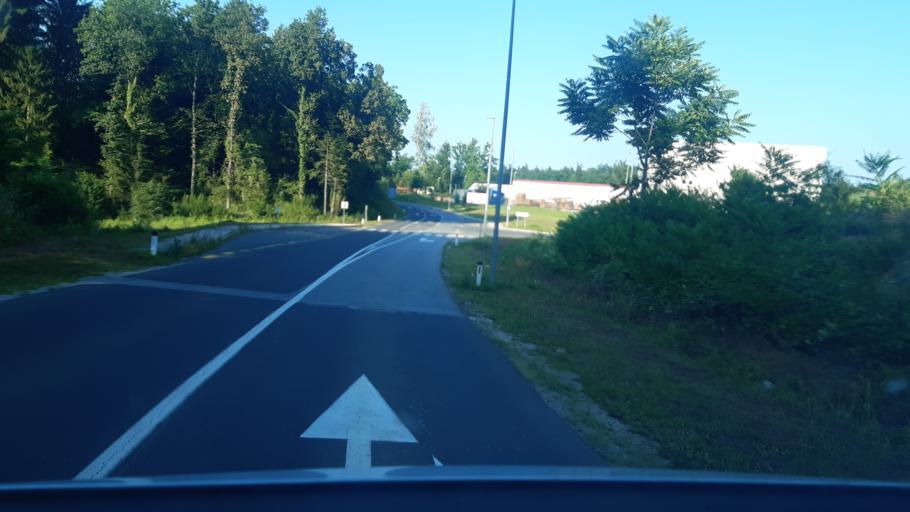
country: SI
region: Crnomelj
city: Crnomelj
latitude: 45.5569
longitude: 15.1670
